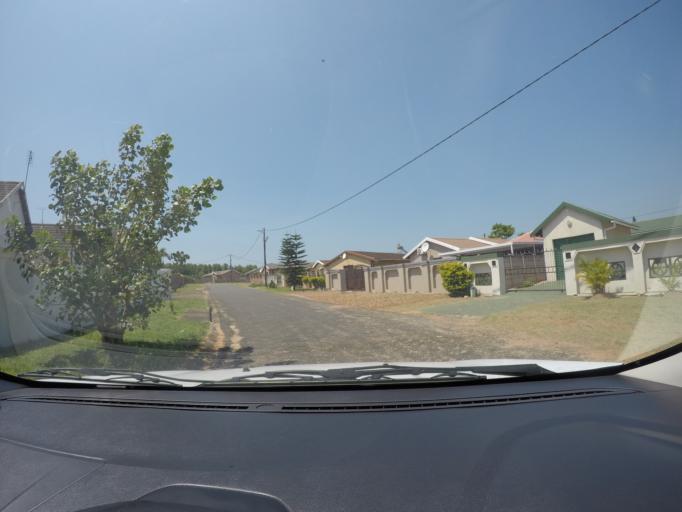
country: ZA
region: KwaZulu-Natal
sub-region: uThungulu District Municipality
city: eSikhawini
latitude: -28.8700
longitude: 31.9242
